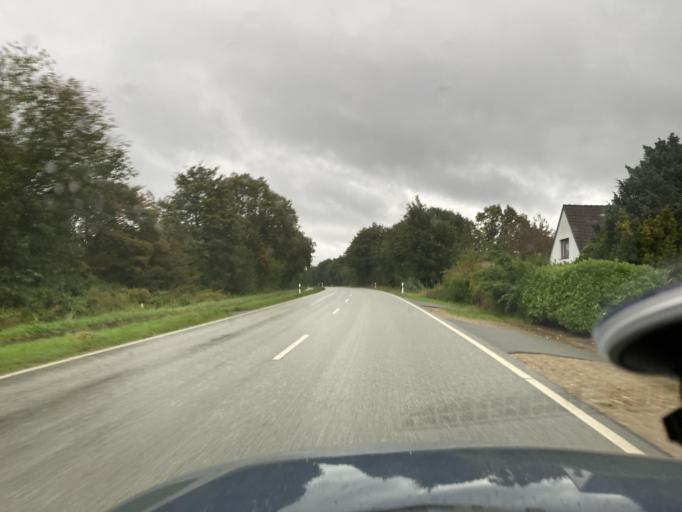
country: DE
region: Schleswig-Holstein
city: Suderdorf
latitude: 54.2184
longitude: 9.3318
